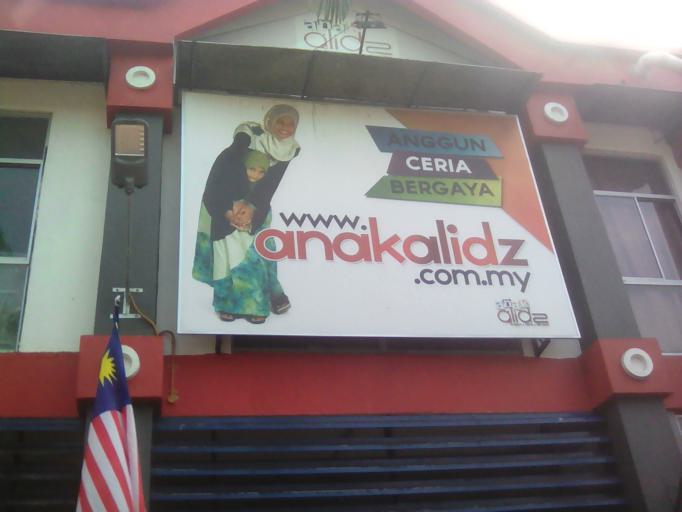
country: MY
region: Kedah
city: Kulim
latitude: 5.3889
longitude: 100.5671
